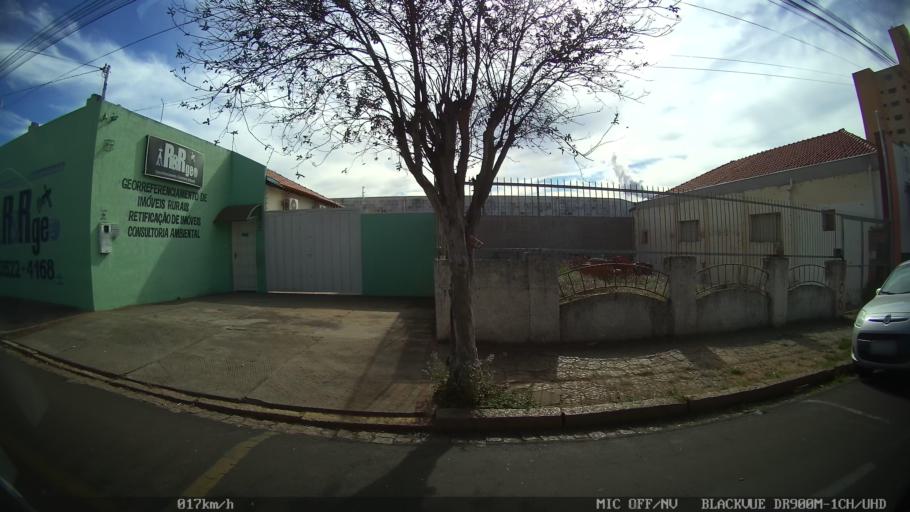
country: BR
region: Sao Paulo
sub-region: Catanduva
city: Catanduva
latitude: -21.1329
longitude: -48.9780
